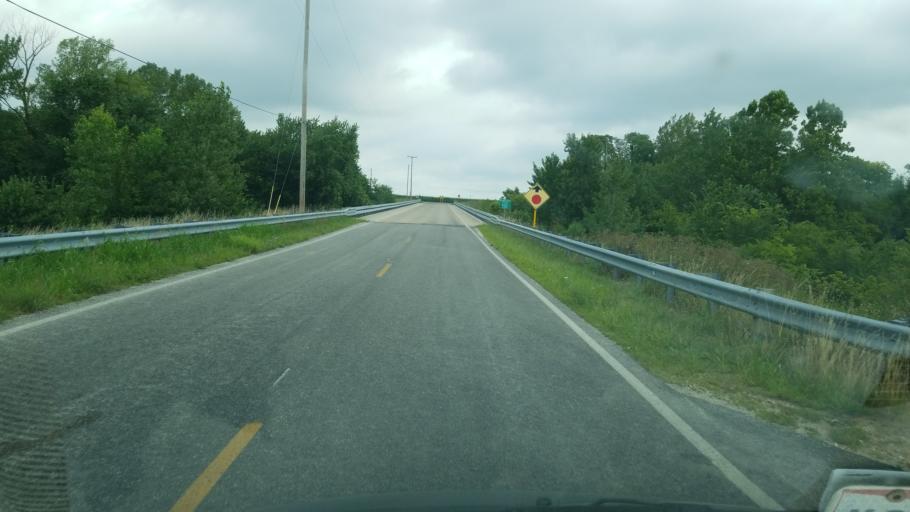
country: US
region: Ohio
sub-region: Seneca County
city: Tiffin
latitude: 41.2086
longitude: -83.1463
